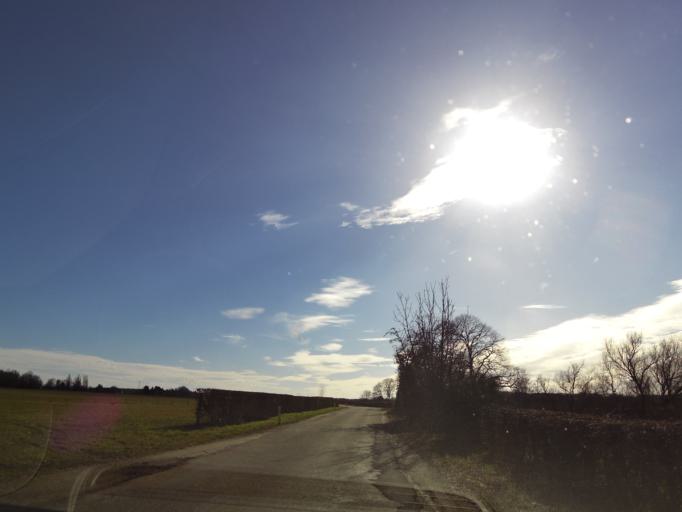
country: NL
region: Limburg
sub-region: Valkenburg aan de Geul
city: Schin op Geul
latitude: 50.7917
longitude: 5.8811
